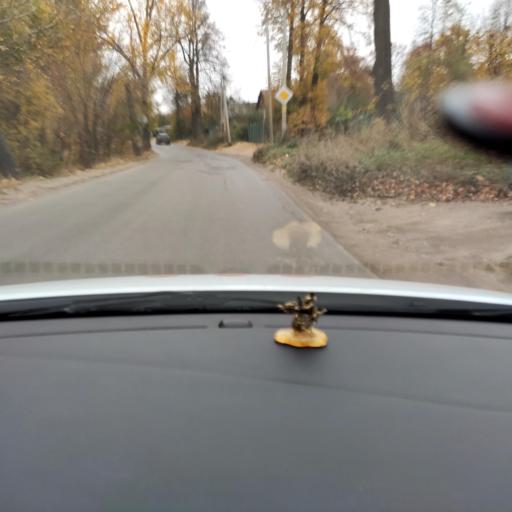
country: RU
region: Tatarstan
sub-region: Gorod Kazan'
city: Kazan
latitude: 55.7271
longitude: 49.1582
